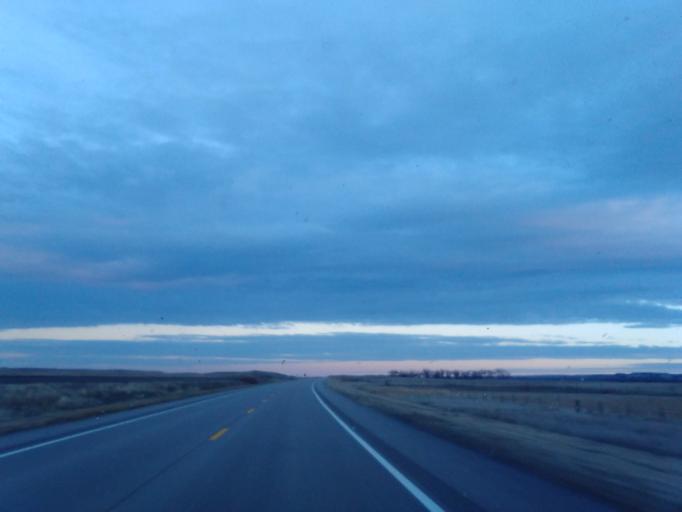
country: US
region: Nebraska
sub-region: Garden County
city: Oshkosh
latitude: 41.3823
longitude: -102.2742
